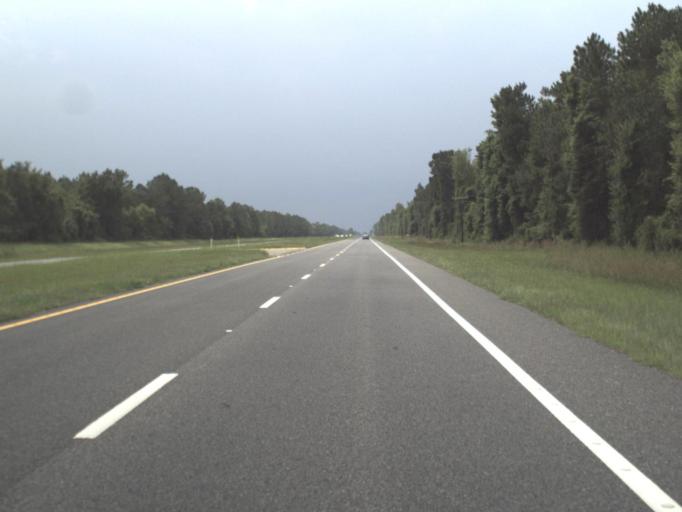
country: US
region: Florida
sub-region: Levy County
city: Chiefland
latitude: 29.3469
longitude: -82.7805
